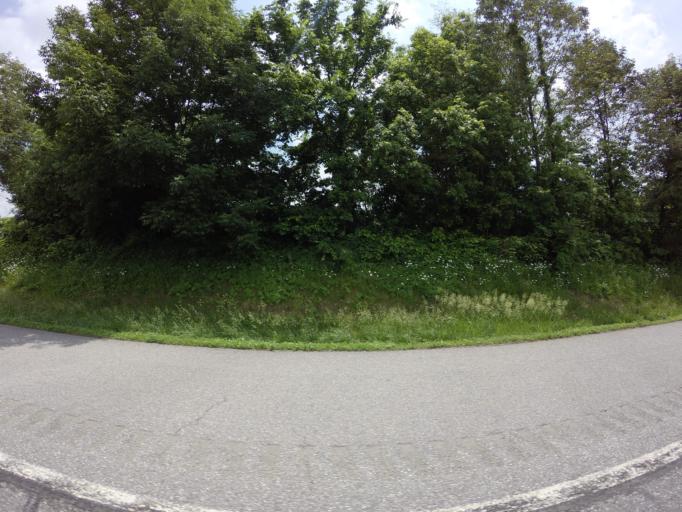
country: US
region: Maryland
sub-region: Frederick County
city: Brunswick
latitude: 39.3515
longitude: -77.6149
